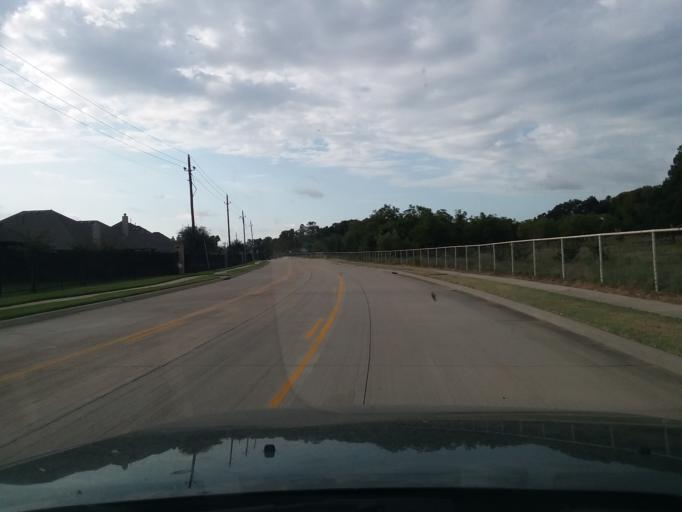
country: US
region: Texas
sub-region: Denton County
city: Hickory Creek
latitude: 33.1254
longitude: -97.0604
